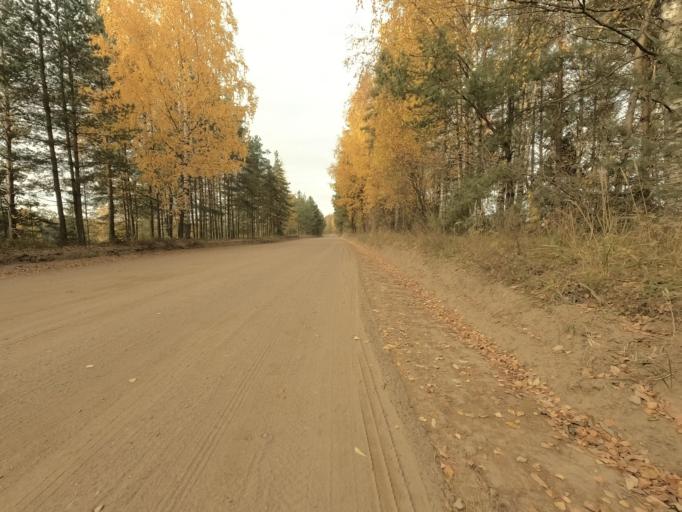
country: RU
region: Leningrad
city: Priladozhskiy
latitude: 59.6747
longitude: 31.3663
